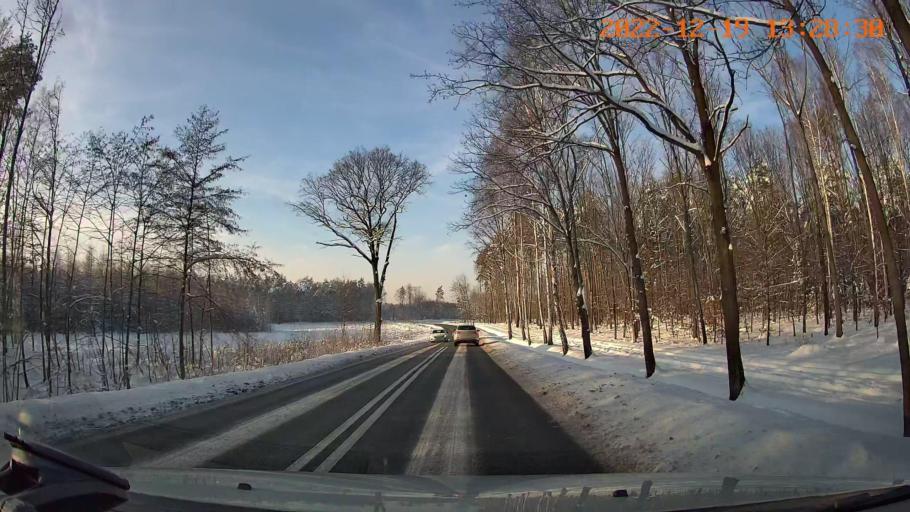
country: PL
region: Silesian Voivodeship
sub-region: Powiat bierunsko-ledzinski
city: Ledziny
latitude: 50.1121
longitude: 19.1273
